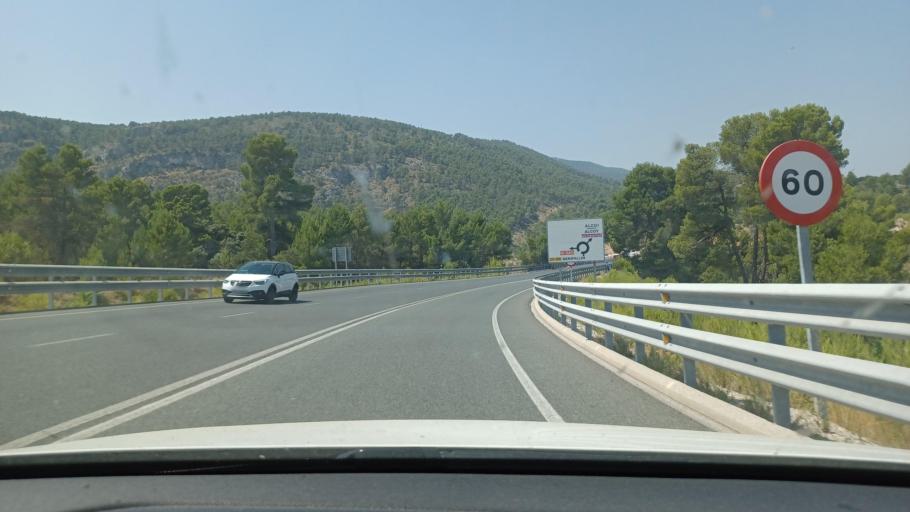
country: ES
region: Valencia
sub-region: Provincia de Alicante
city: Alcoy
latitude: 38.6810
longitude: -0.4633
